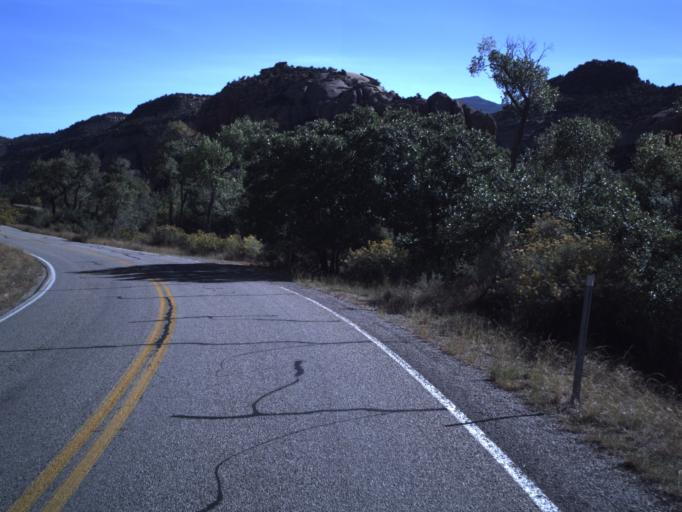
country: US
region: Utah
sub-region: San Juan County
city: Monticello
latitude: 38.0115
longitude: -109.5389
